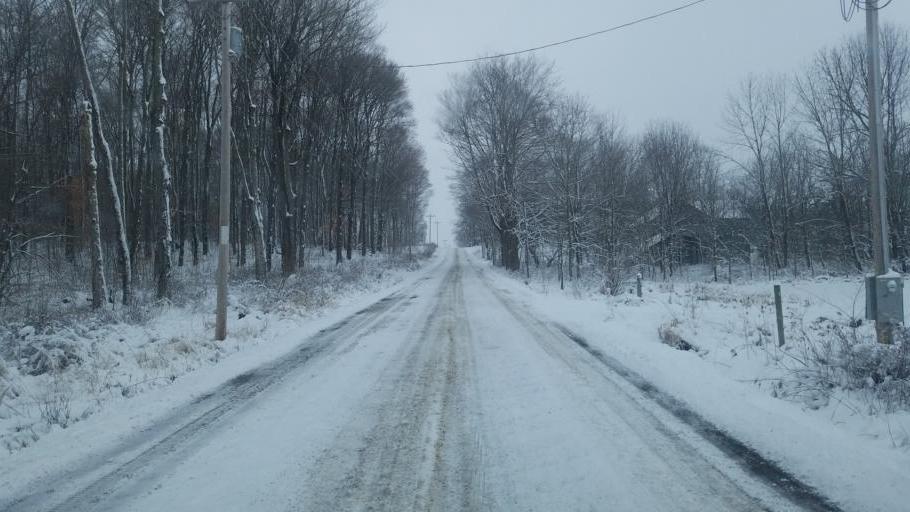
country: US
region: Ohio
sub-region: Knox County
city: Fredericktown
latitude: 40.5207
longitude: -82.6717
